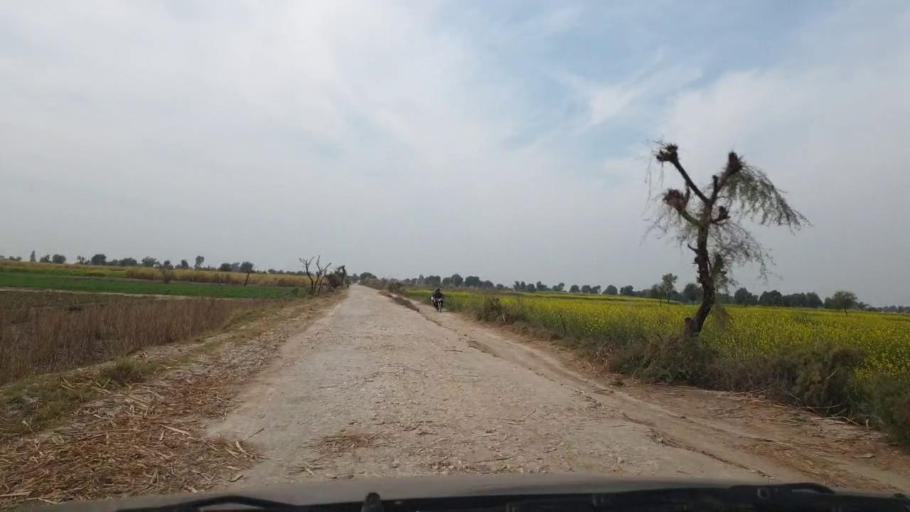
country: PK
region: Sindh
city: Sinjhoro
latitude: 26.0828
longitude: 68.8251
